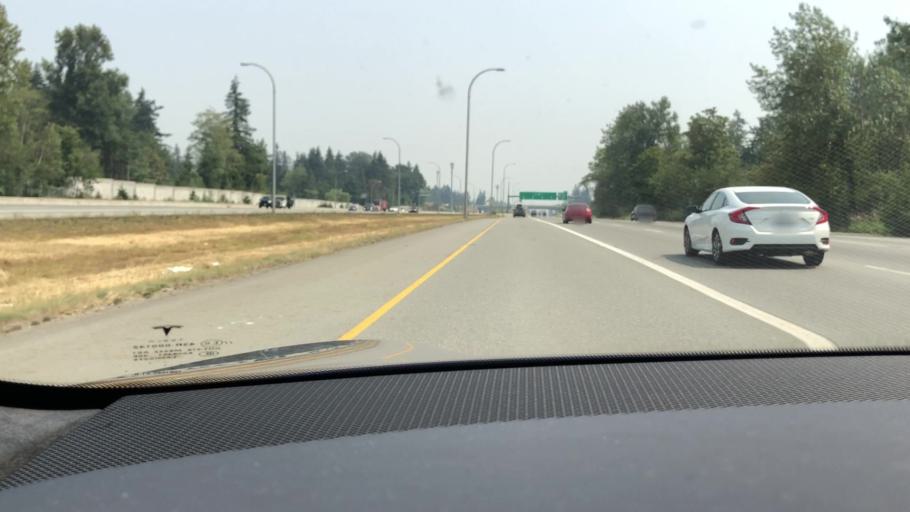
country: CA
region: British Columbia
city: Pitt Meadows
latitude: 49.1841
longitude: -122.7457
